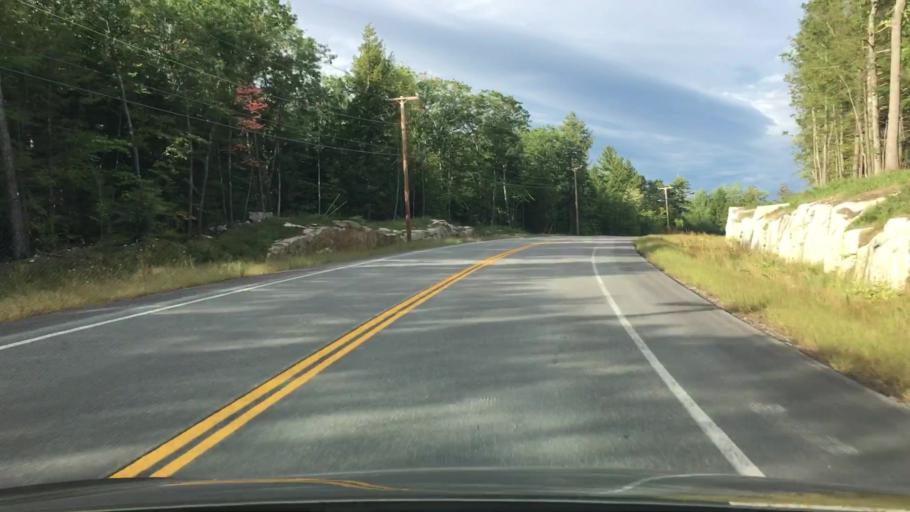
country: US
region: Maine
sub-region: Oxford County
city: Lovell
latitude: 44.0378
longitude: -70.8861
